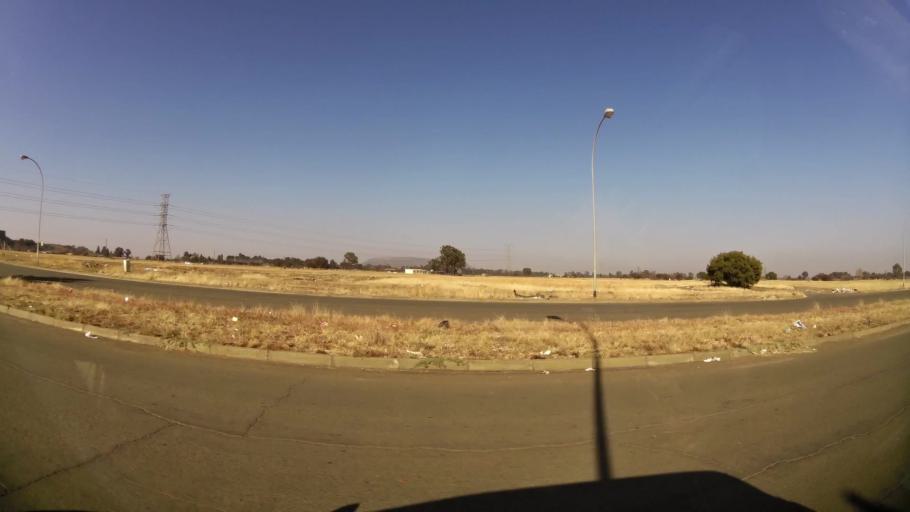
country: ZA
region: Orange Free State
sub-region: Mangaung Metropolitan Municipality
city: Bloemfontein
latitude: -29.1851
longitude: 26.1839
